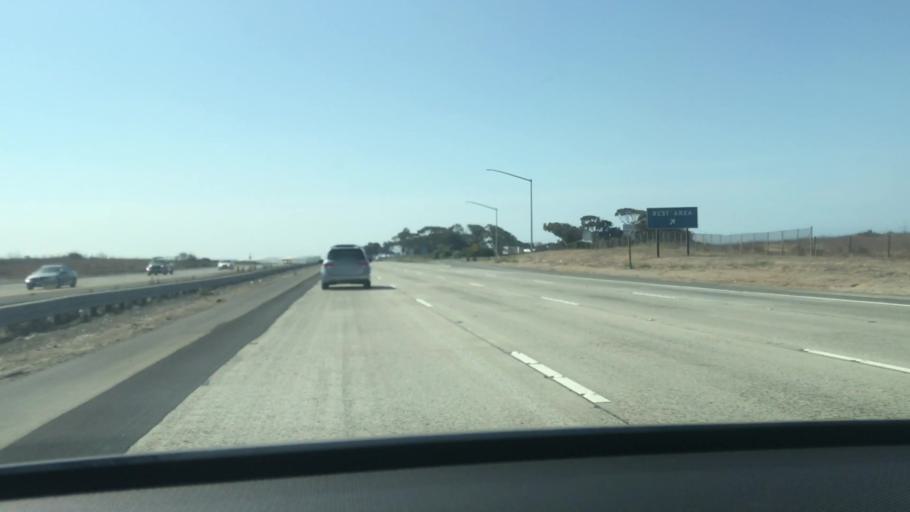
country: US
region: California
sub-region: San Diego County
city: Camp Pendleton South
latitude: 33.2767
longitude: -117.4458
